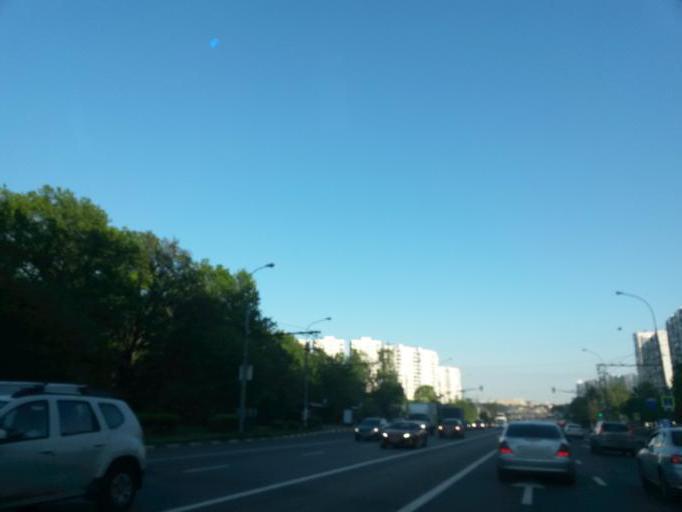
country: RU
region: Moscow
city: Biryulevo
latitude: 55.5853
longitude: 37.6782
